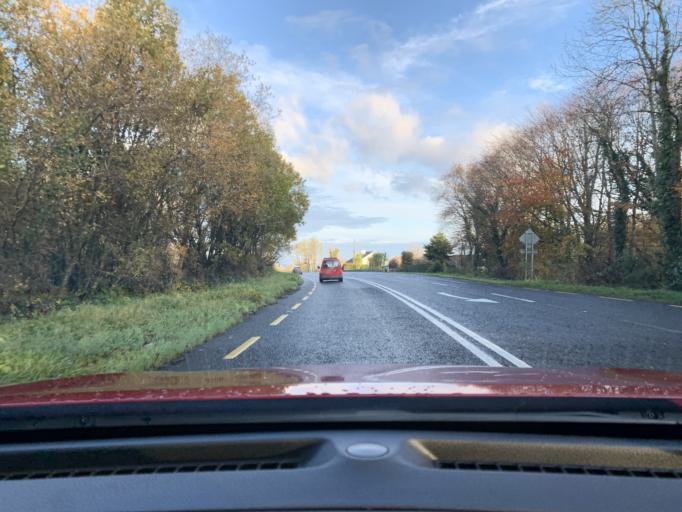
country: IE
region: Connaught
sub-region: Sligo
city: Sligo
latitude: 54.3819
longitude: -8.5289
